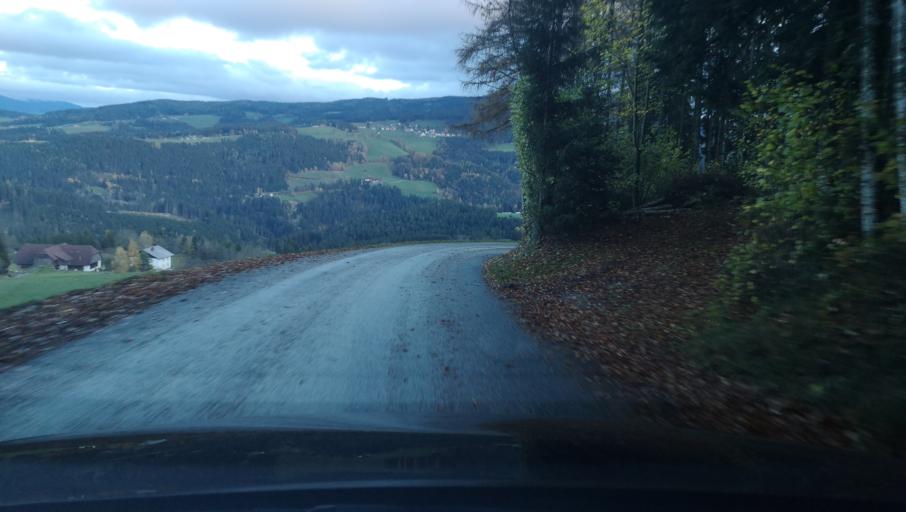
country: AT
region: Styria
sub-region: Politischer Bezirk Weiz
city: Birkfeld
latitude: 47.3355
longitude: 15.6717
